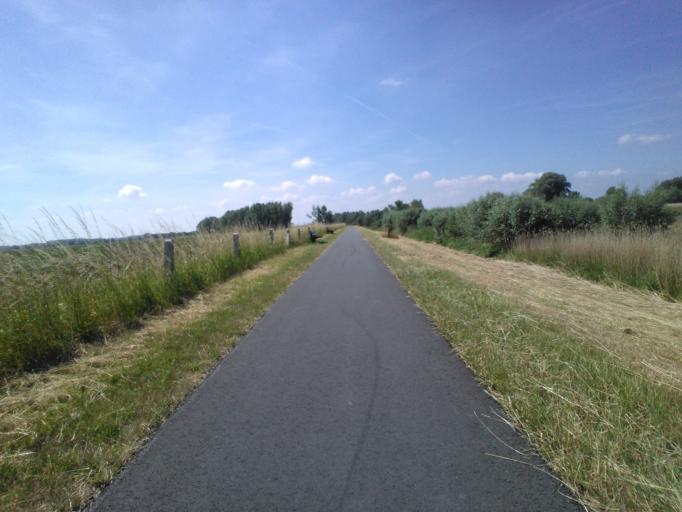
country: NL
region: North Brabant
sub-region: Gemeente Werkendam
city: Werkendam
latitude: 51.7941
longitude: 4.8765
